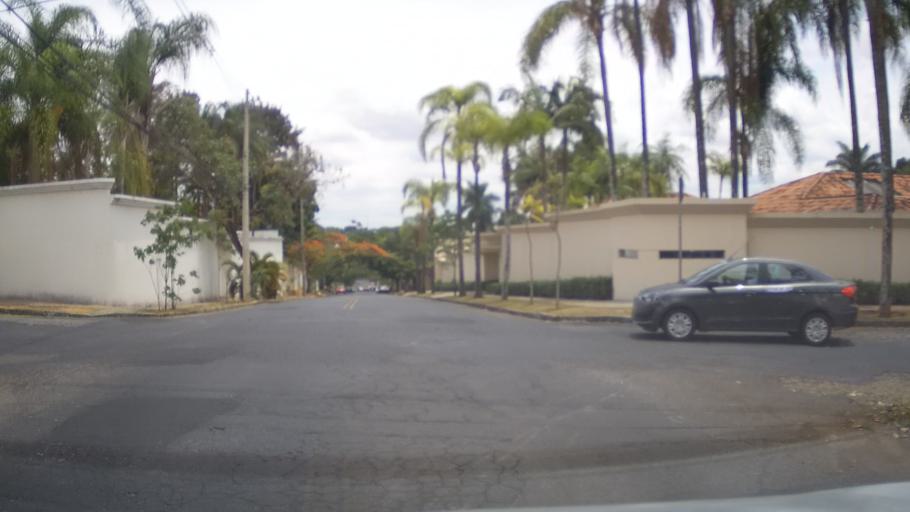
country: BR
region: Minas Gerais
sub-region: Belo Horizonte
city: Belo Horizonte
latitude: -19.8554
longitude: -43.9645
